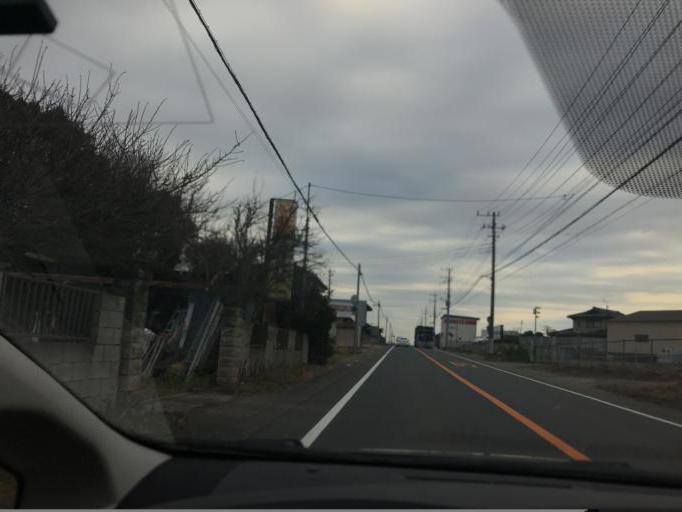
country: JP
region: Ibaraki
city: Mitsukaido
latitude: 36.0297
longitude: 140.0276
